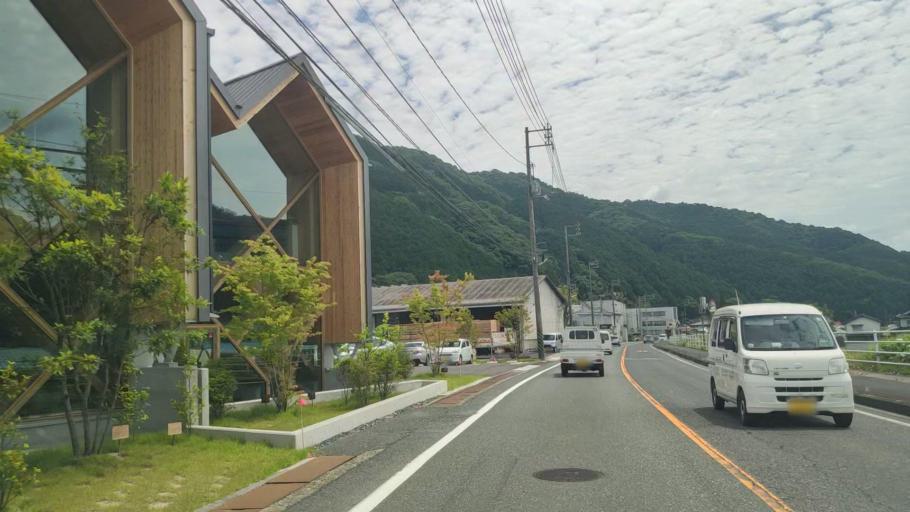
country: JP
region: Okayama
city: Niimi
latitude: 35.0846
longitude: 133.6992
